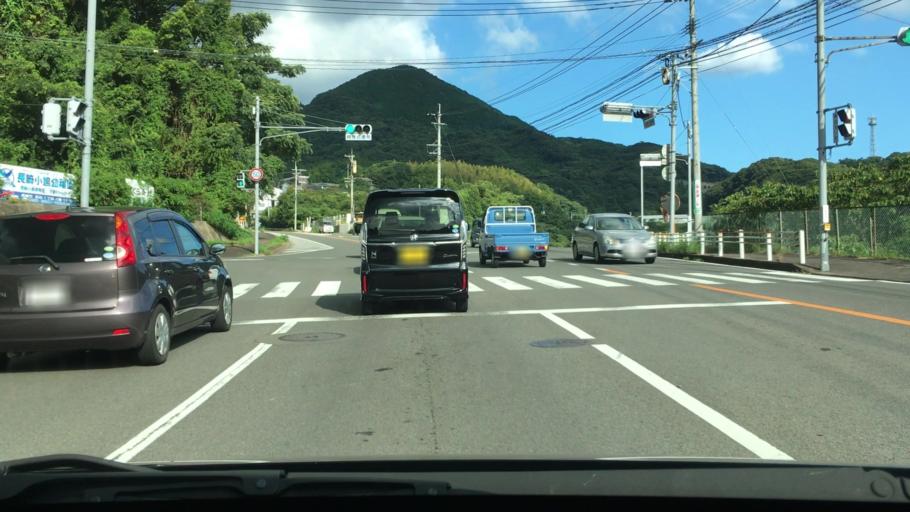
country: JP
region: Nagasaki
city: Togitsu
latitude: 32.8176
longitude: 129.8037
